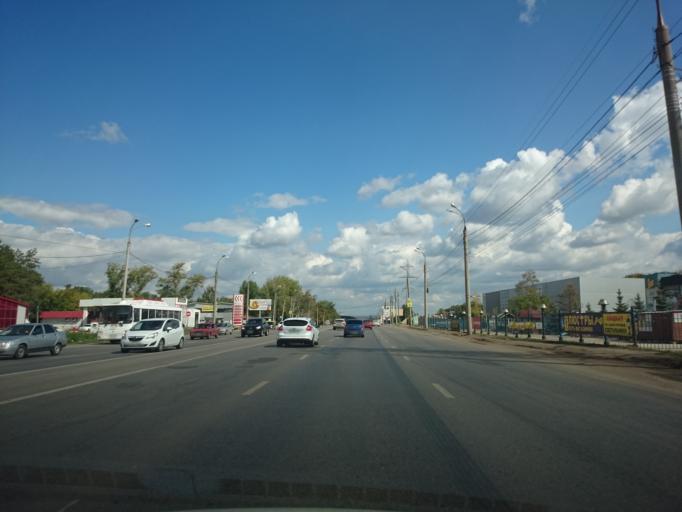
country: RU
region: Samara
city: Samara
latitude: 53.2629
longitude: 50.2425
